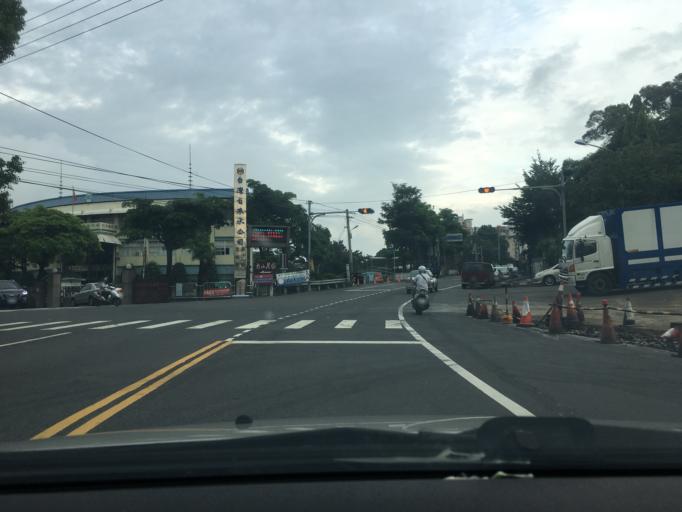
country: TW
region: Taiwan
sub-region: Changhua
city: Chang-hua
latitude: 24.0745
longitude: 120.5559
